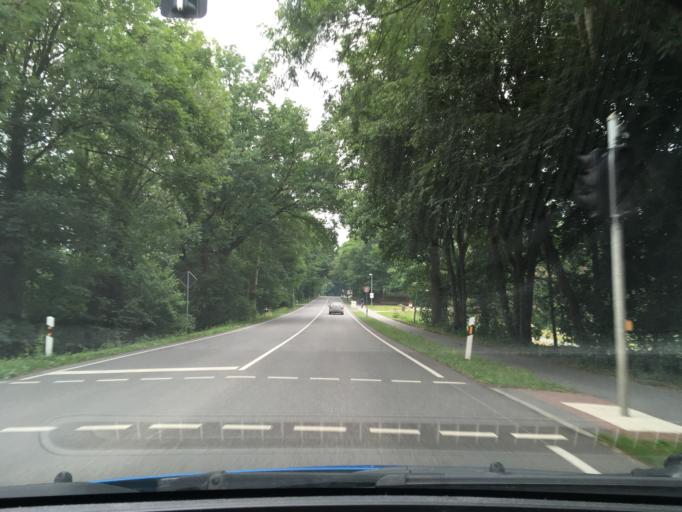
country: DE
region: Lower Saxony
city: Wenzendorf
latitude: 53.3831
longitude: 9.7993
